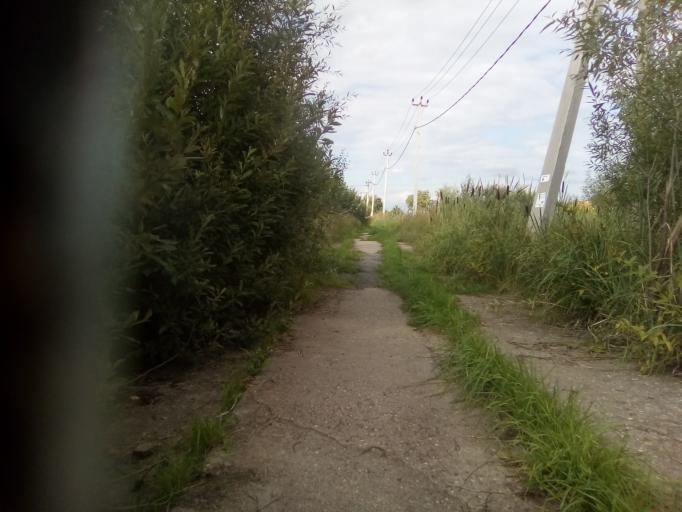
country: RU
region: Moskovskaya
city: Zhavoronki
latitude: 55.6507
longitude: 37.1497
